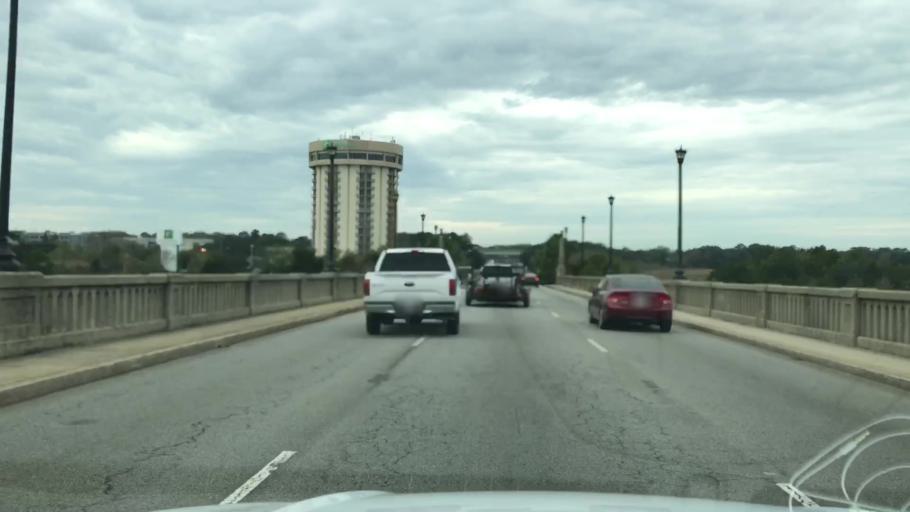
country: US
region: South Carolina
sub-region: Charleston County
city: Charleston
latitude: 32.7828
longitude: -79.9627
